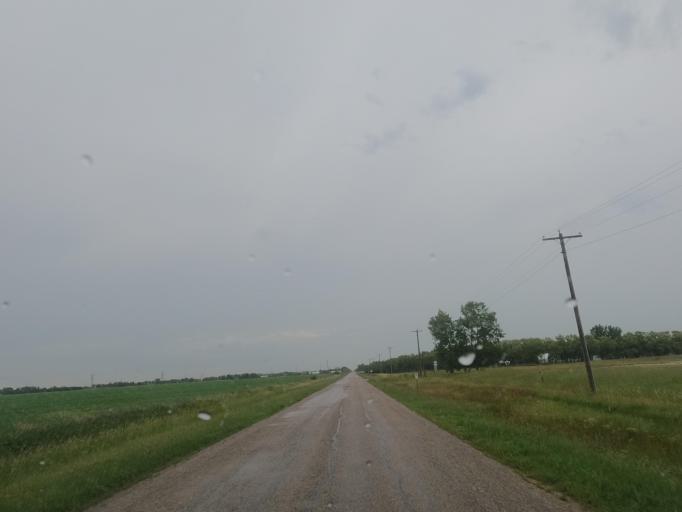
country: CA
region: Manitoba
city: Winnipeg
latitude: 49.8323
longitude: -96.9812
